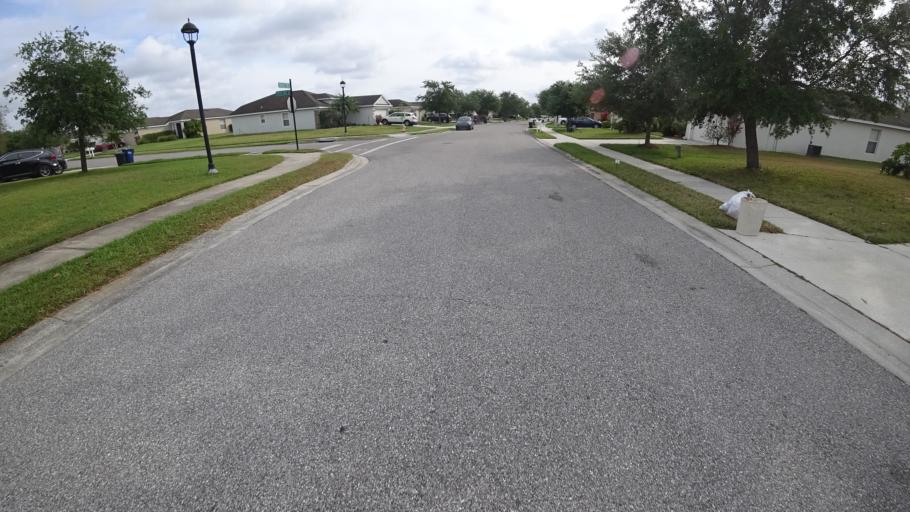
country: US
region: Florida
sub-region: Manatee County
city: Ellenton
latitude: 27.5583
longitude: -82.4627
